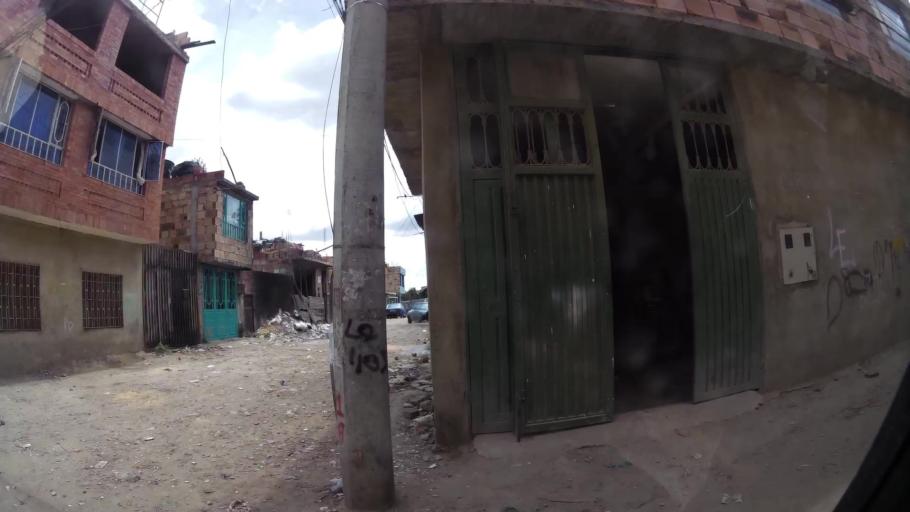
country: CO
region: Cundinamarca
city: Funza
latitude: 4.7202
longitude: -74.1340
